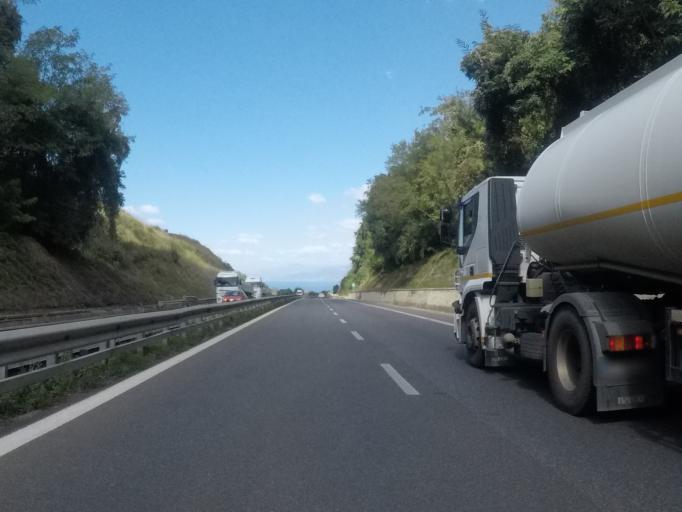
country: IT
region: Calabria
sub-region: Provincia di Vibo-Valentia
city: Sant'Onofrio
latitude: 38.7096
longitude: 16.1539
